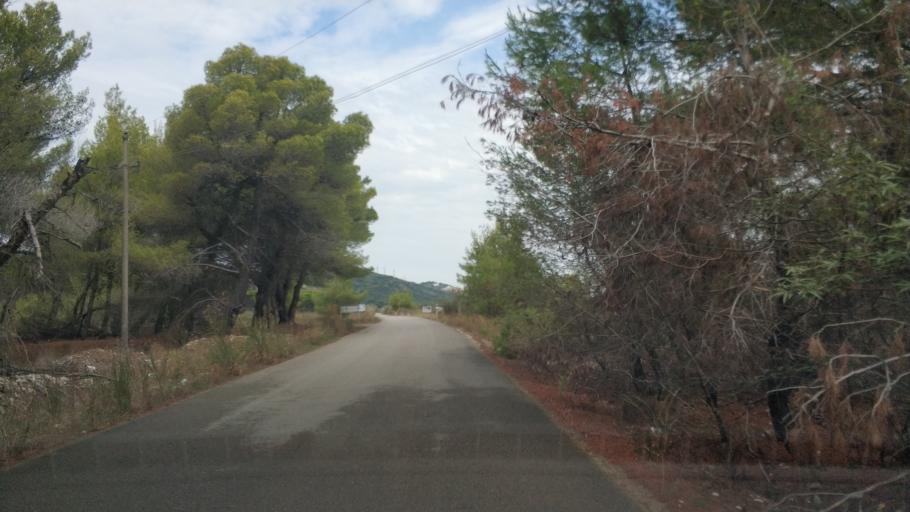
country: AL
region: Vlore
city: Vlore
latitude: 40.5011
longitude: 19.4285
